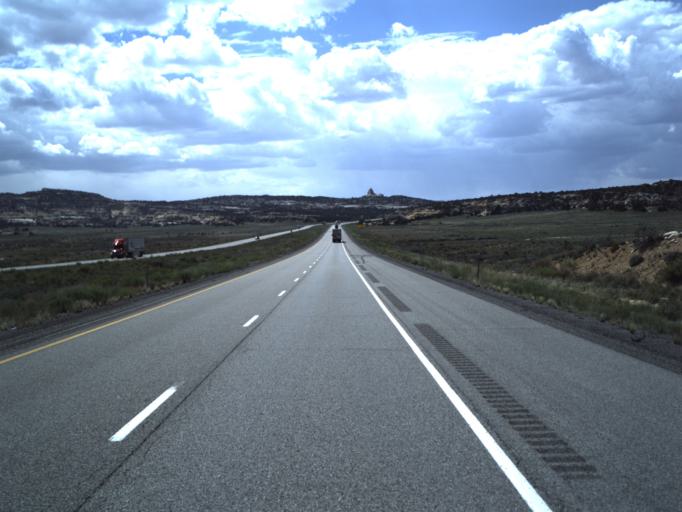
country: US
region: Utah
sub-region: Emery County
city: Castle Dale
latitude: 38.8688
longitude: -110.7775
